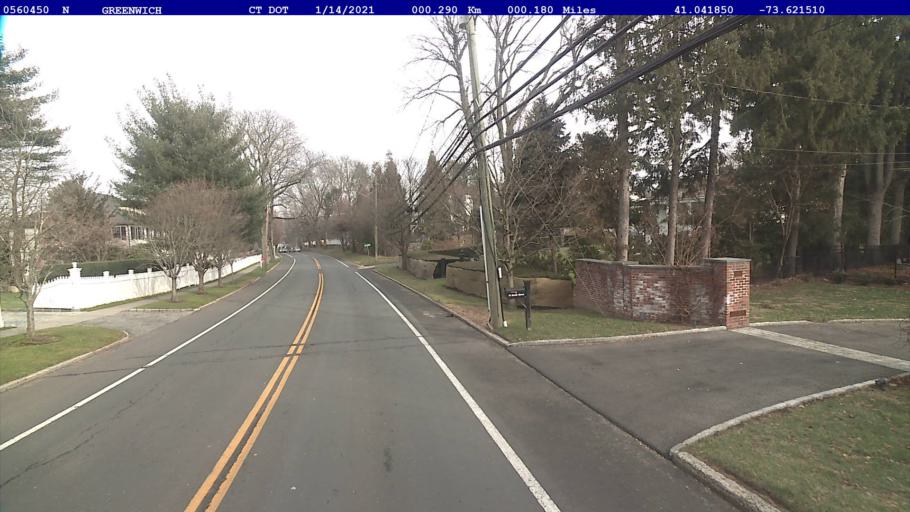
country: US
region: Connecticut
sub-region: Fairfield County
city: Greenwich
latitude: 41.0419
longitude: -73.6215
